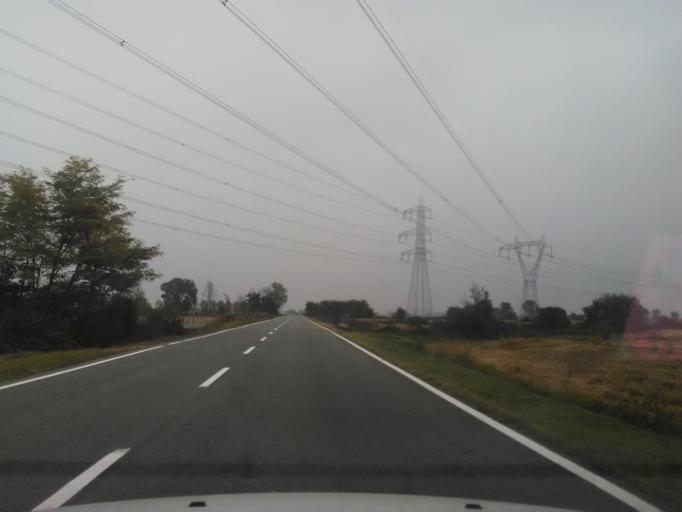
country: IT
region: Piedmont
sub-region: Provincia di Vercelli
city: Ronsecco
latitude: 45.2585
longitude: 8.2291
